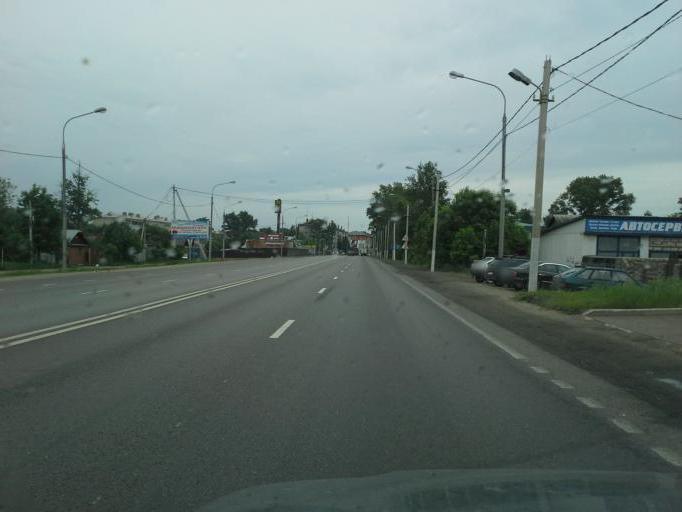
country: RU
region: Vladimir
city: Pokrov
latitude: 55.9165
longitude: 39.1654
